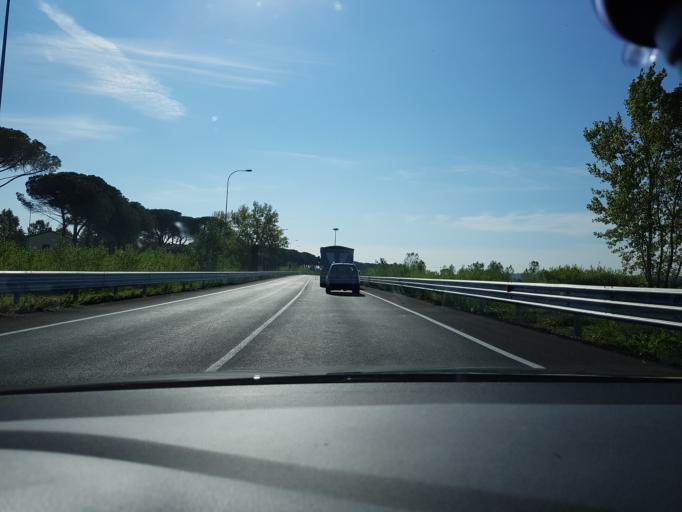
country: IT
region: Tuscany
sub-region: Province of Pisa
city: Ponte A Elsa
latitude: 43.6802
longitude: 10.9145
